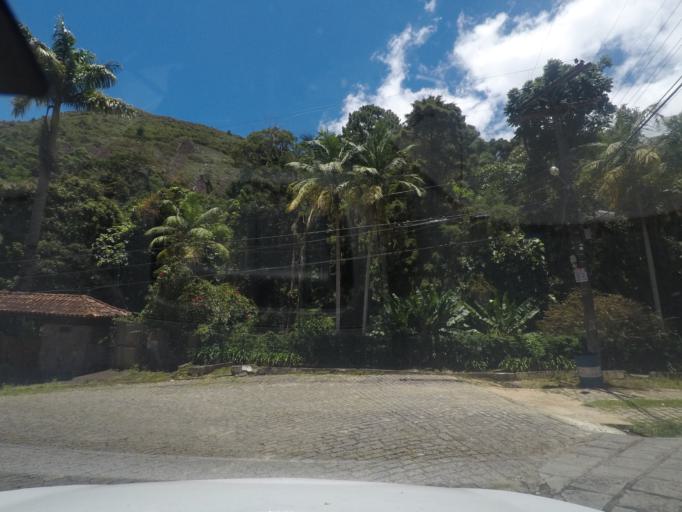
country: BR
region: Rio de Janeiro
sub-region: Teresopolis
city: Teresopolis
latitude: -22.4330
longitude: -42.9951
